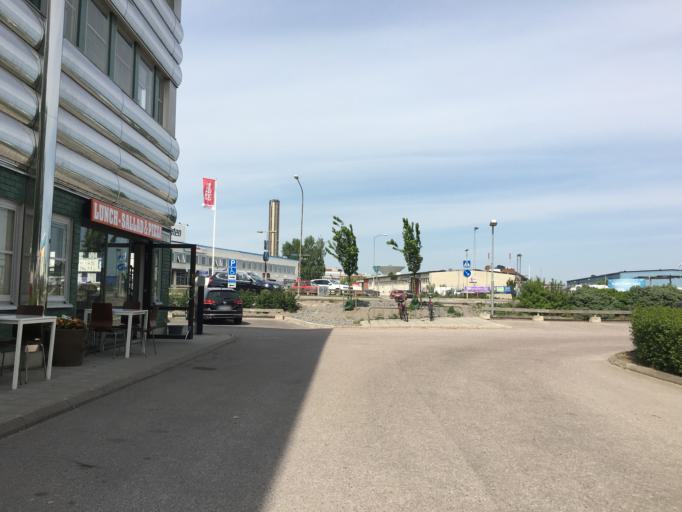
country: SE
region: Uppsala
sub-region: Uppsala Kommun
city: Uppsala
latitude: 59.8463
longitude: 17.6741
